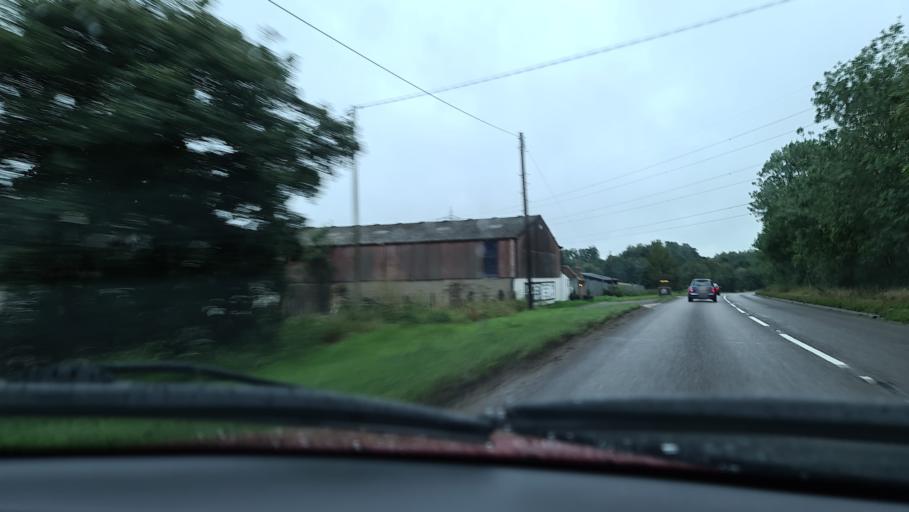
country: GB
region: England
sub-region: Buckinghamshire
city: Seer Green
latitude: 51.6317
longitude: -0.6209
